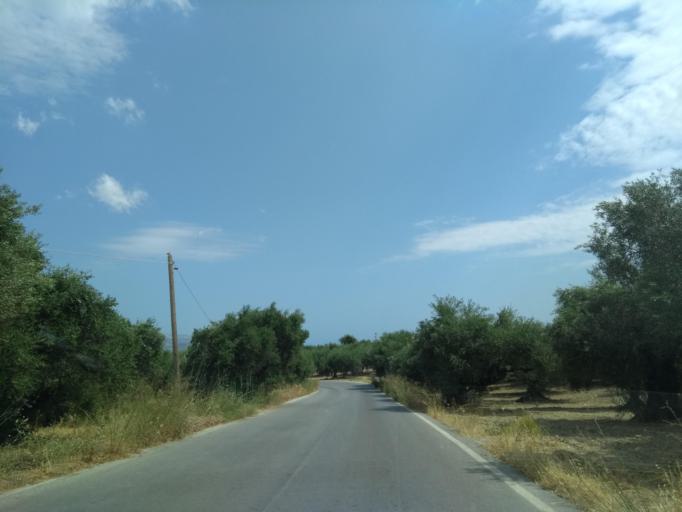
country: GR
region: Crete
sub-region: Nomos Chanias
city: Kalivai
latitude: 35.4464
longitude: 24.1754
